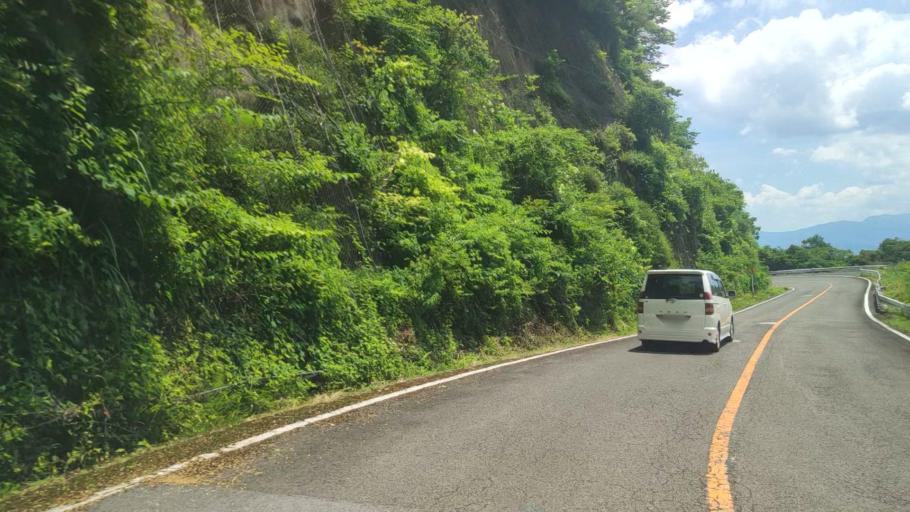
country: JP
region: Gifu
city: Tarui
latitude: 35.3919
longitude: 136.4392
